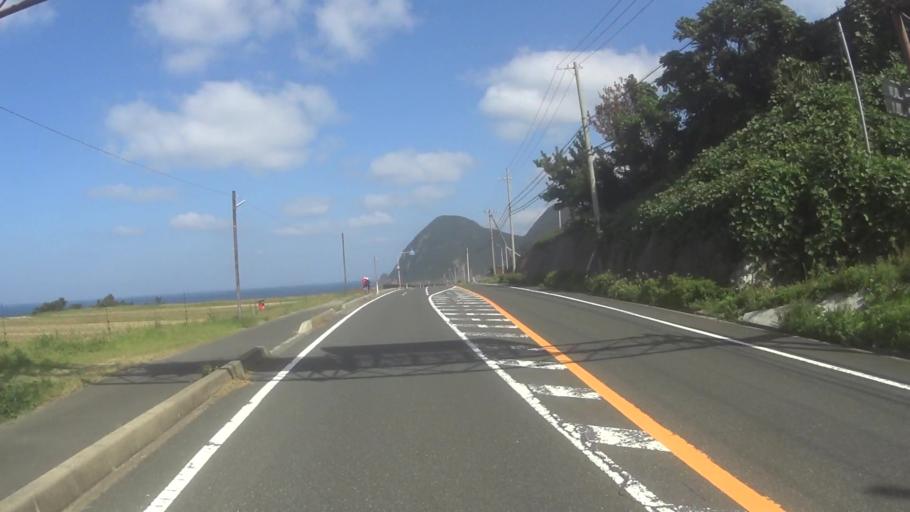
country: JP
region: Kyoto
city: Miyazu
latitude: 35.7426
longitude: 135.1181
